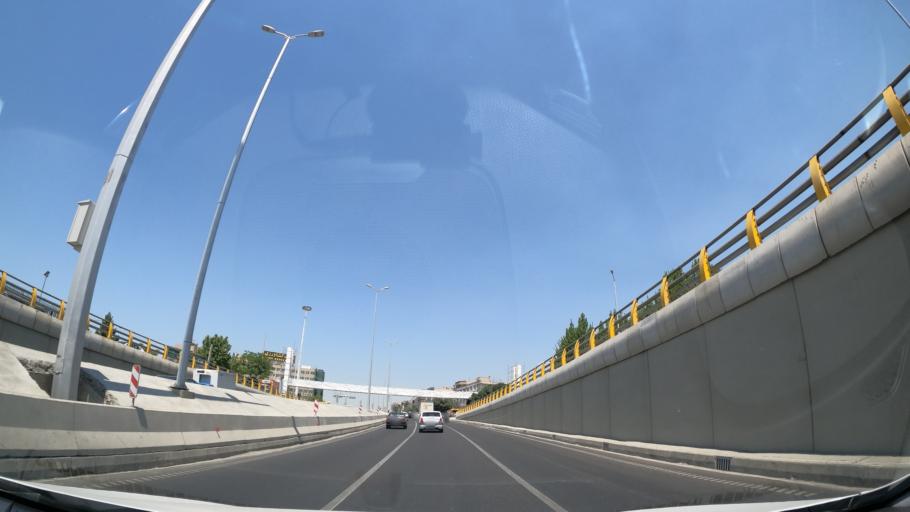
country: IR
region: Tehran
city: Tehran
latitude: 35.7259
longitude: 51.3794
